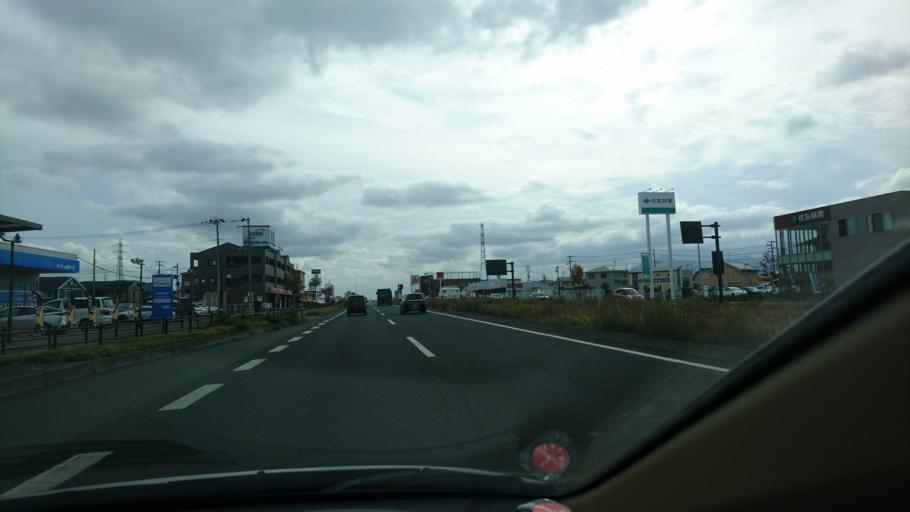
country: JP
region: Iwate
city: Morioka-shi
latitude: 39.6834
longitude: 141.1357
